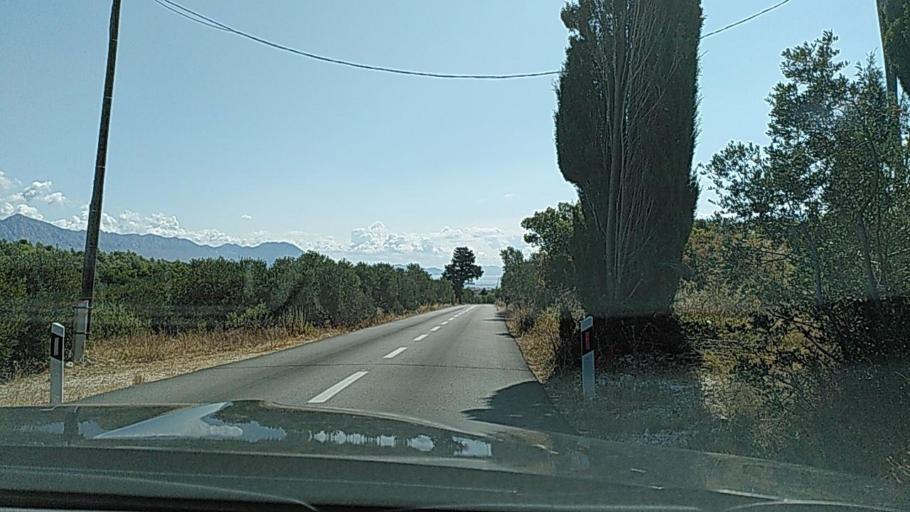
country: HR
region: Dubrovacko-Neretvanska
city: Orebic
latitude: 43.1315
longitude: 17.1719
